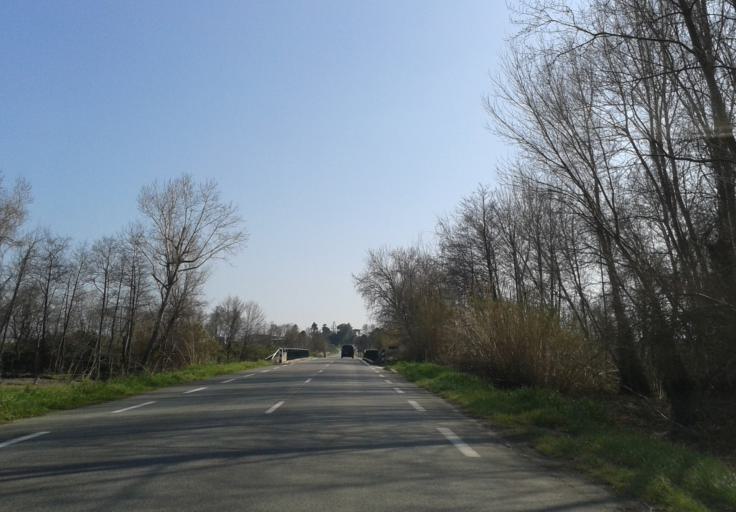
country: FR
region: Corsica
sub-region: Departement de la Haute-Corse
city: Cervione
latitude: 42.2892
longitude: 9.5488
